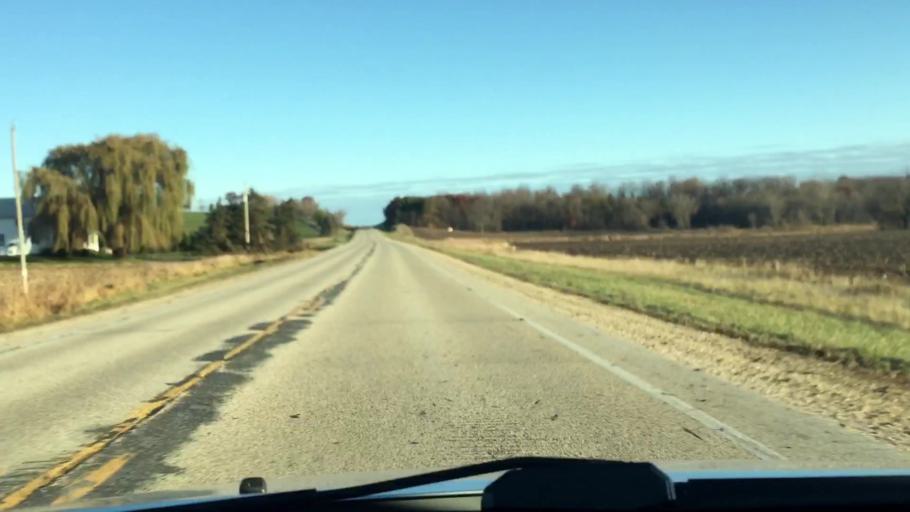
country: US
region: Wisconsin
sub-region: Dodge County
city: Theresa
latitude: 43.4584
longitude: -88.4503
